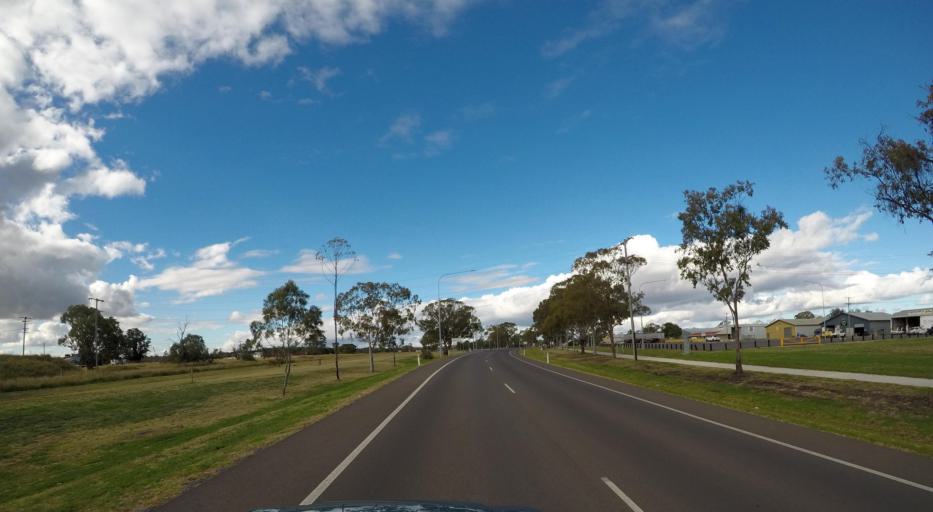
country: AU
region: Queensland
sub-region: Toowoomba
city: Westbrook
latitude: -27.7182
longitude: 151.6220
